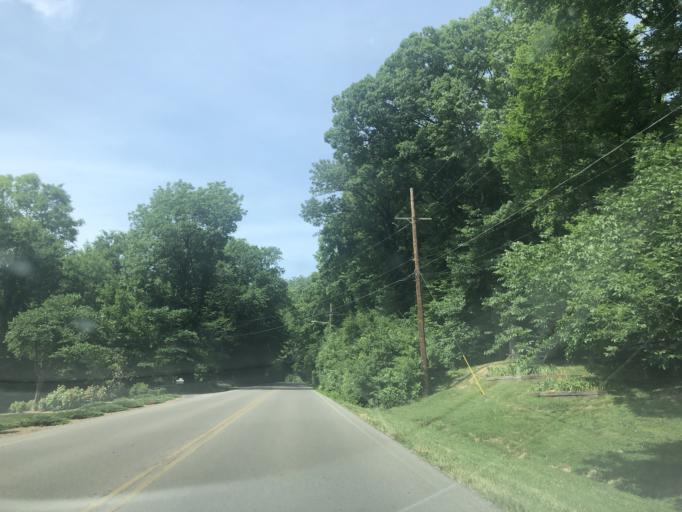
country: US
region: Tennessee
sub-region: Davidson County
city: Forest Hills
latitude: 36.0724
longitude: -86.8258
